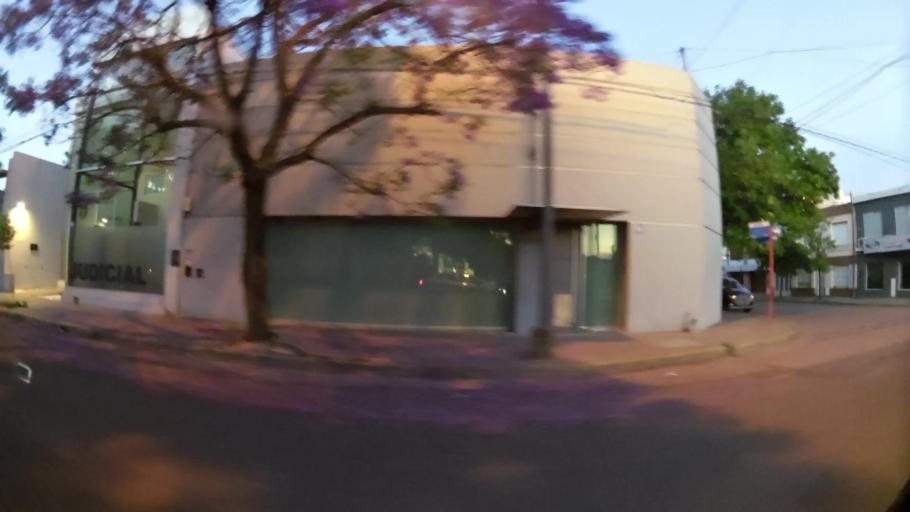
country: AR
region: Cordoba
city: Villa Maria
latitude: -32.4080
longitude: -63.2481
